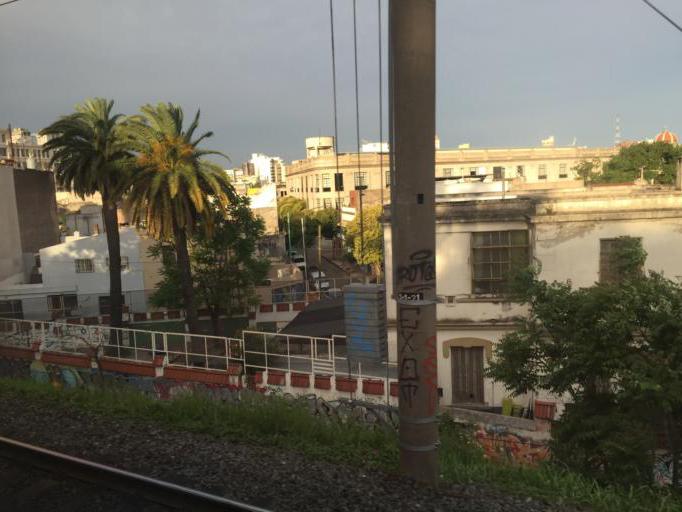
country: AR
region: Buenos Aires
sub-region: Partido de Avellaneda
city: Avellaneda
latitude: -34.6409
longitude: -58.3806
